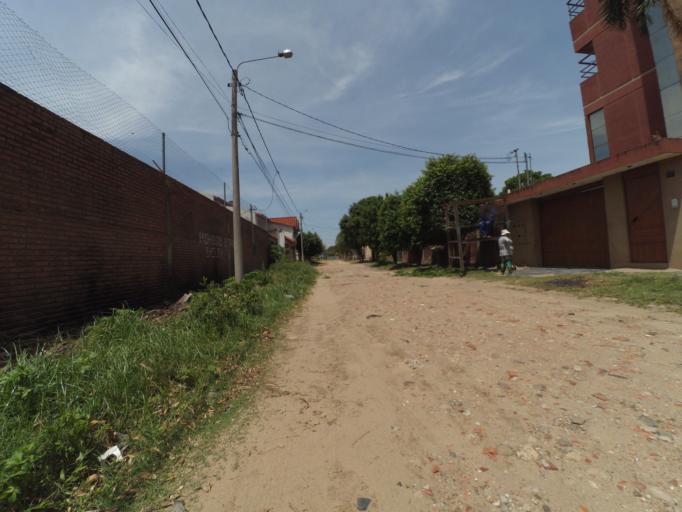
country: BO
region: Santa Cruz
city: Santa Cruz de la Sierra
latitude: -17.8214
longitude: -63.2226
